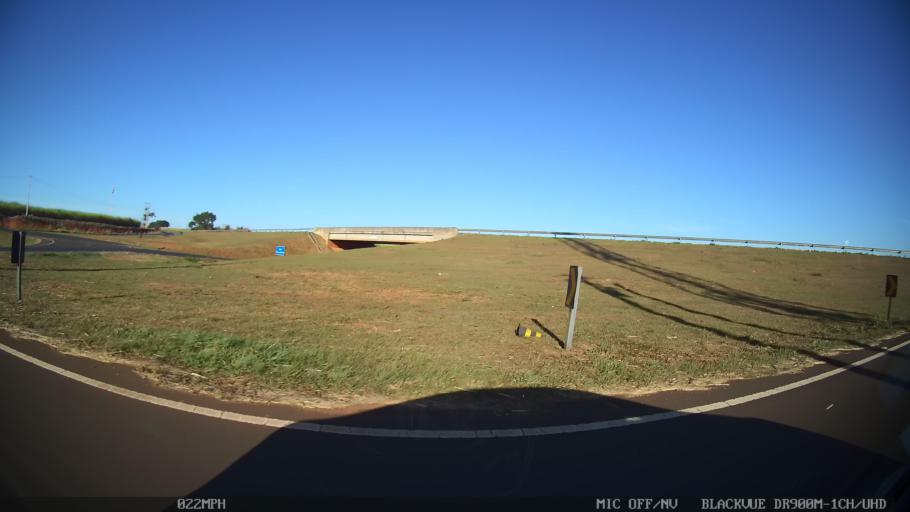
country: BR
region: Sao Paulo
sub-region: Guapiacu
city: Guapiacu
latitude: -20.7372
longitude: -49.0822
